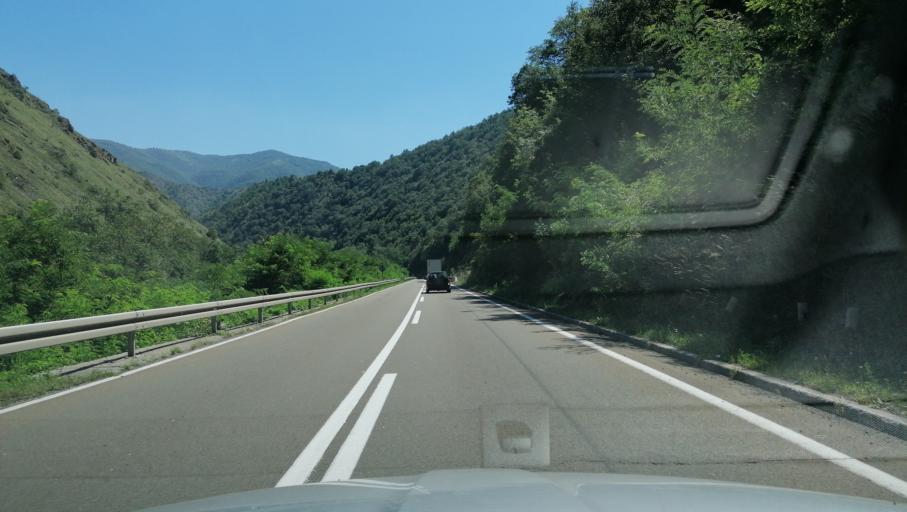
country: RS
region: Central Serbia
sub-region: Raski Okrug
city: Kraljevo
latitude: 43.5644
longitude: 20.6035
